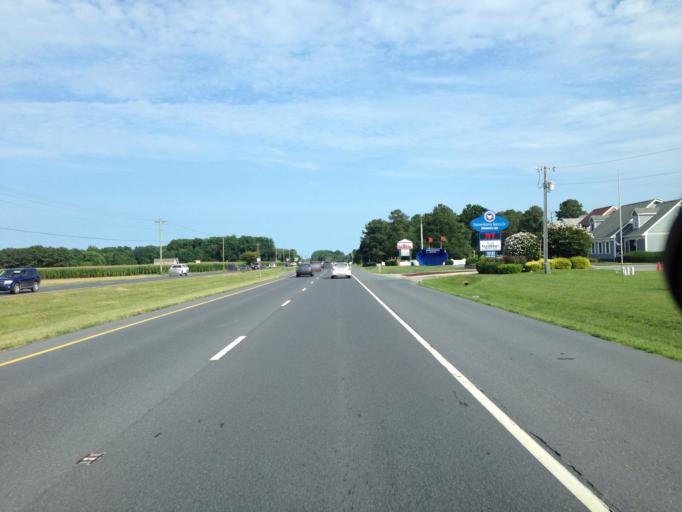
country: US
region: Delaware
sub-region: Sussex County
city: Lewes
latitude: 38.7661
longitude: -75.2123
